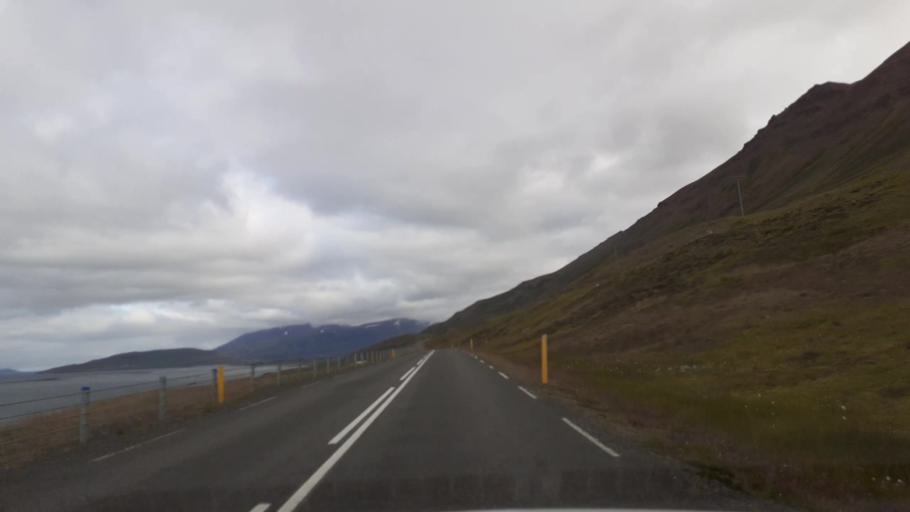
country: IS
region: Northeast
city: Akureyri
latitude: 65.8416
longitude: -18.0567
